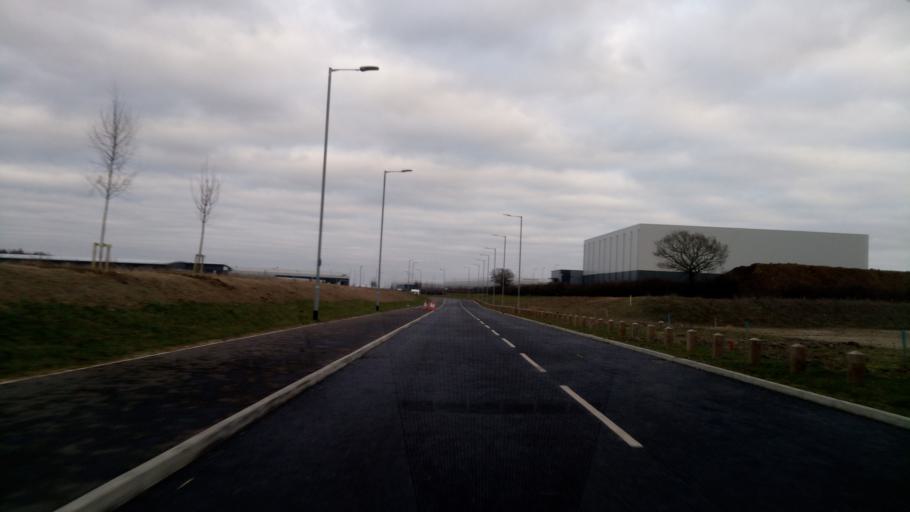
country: GB
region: England
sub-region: Cambridgeshire
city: Stilton
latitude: 52.5332
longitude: -0.3094
